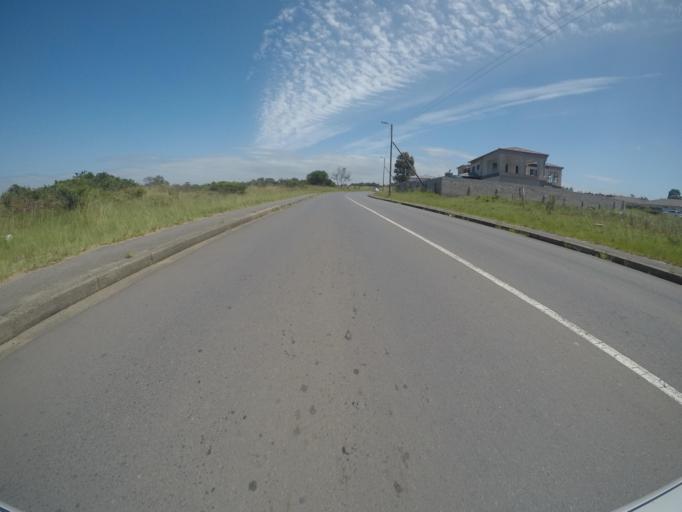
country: ZA
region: Eastern Cape
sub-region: Buffalo City Metropolitan Municipality
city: East London
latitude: -32.9449
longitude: 27.9943
